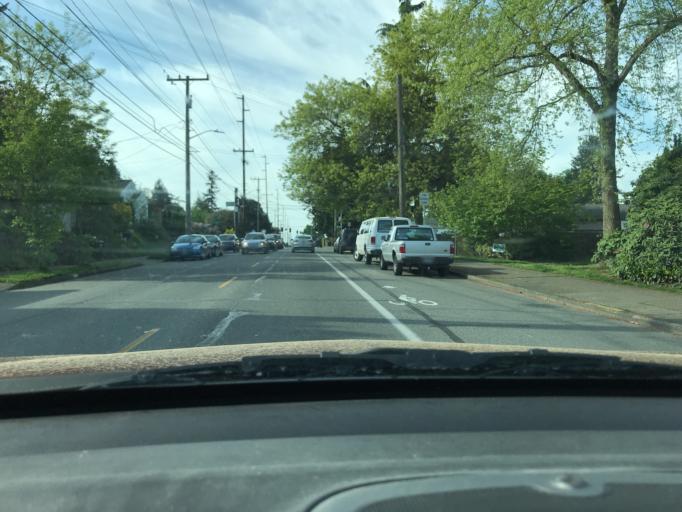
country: US
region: Washington
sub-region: King County
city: Shoreline
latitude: 47.6975
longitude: -122.3231
